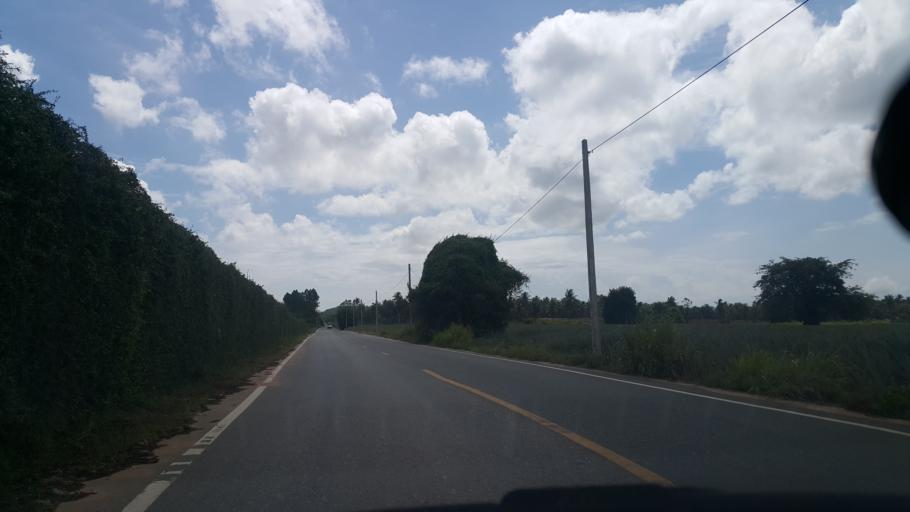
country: TH
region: Rayong
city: Ban Chang
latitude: 12.8073
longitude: 101.0109
